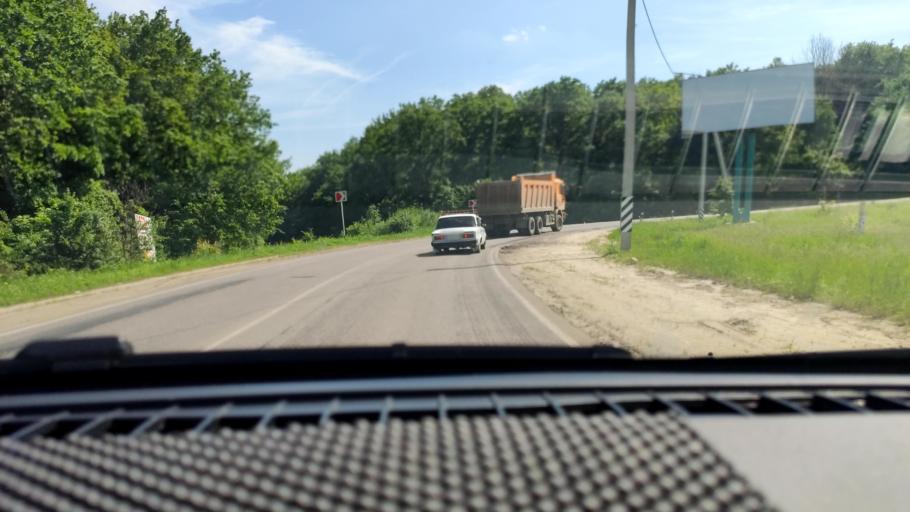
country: RU
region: Voronezj
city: Pridonskoy
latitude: 51.7419
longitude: 39.0530
